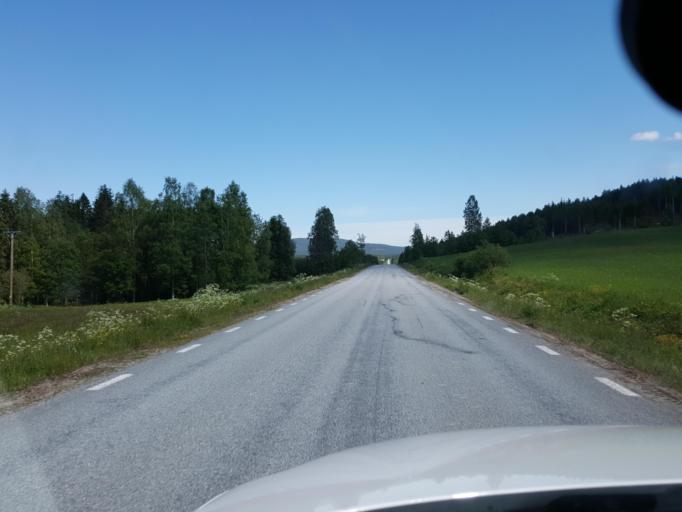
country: SE
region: Gaevleborg
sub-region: Ljusdals Kommun
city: Jaervsoe
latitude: 61.6790
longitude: 16.2155
